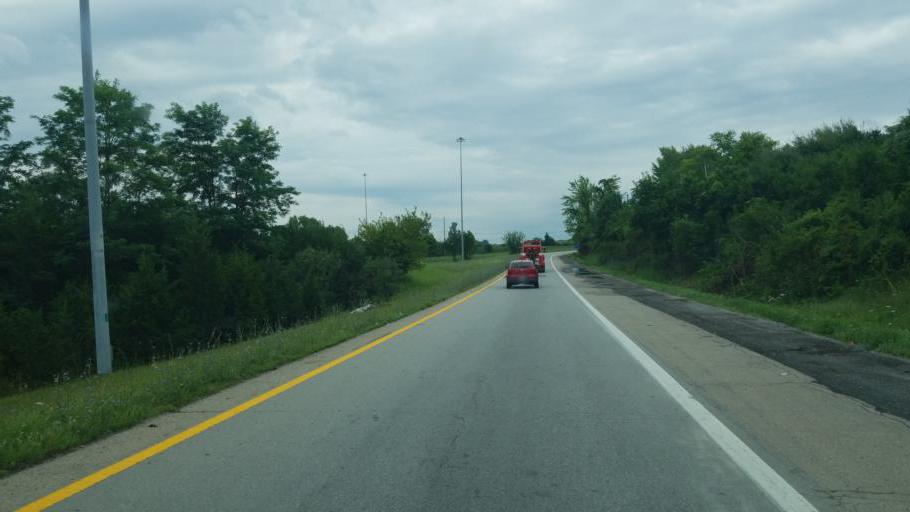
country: US
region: Ohio
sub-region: Franklin County
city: Obetz
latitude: 39.8747
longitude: -83.0067
